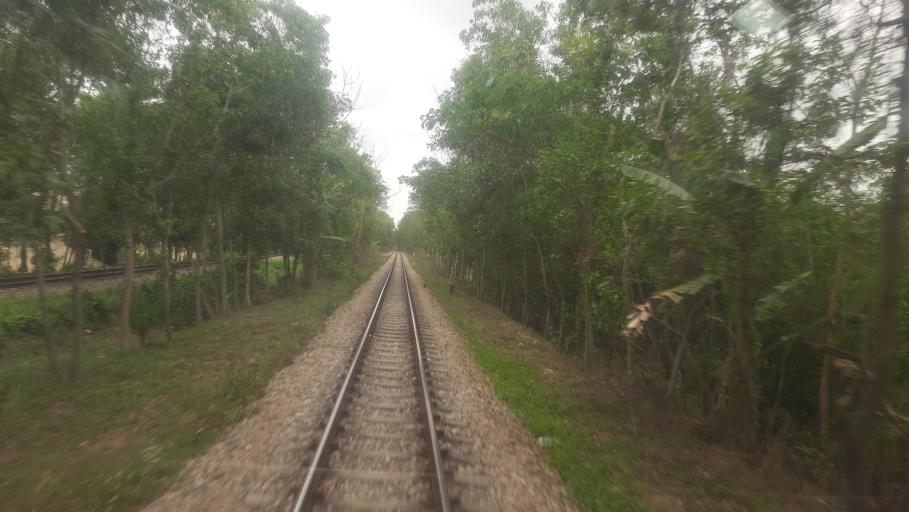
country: BD
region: Chittagong
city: Chhagalnaiya
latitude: 22.9125
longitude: 91.5295
